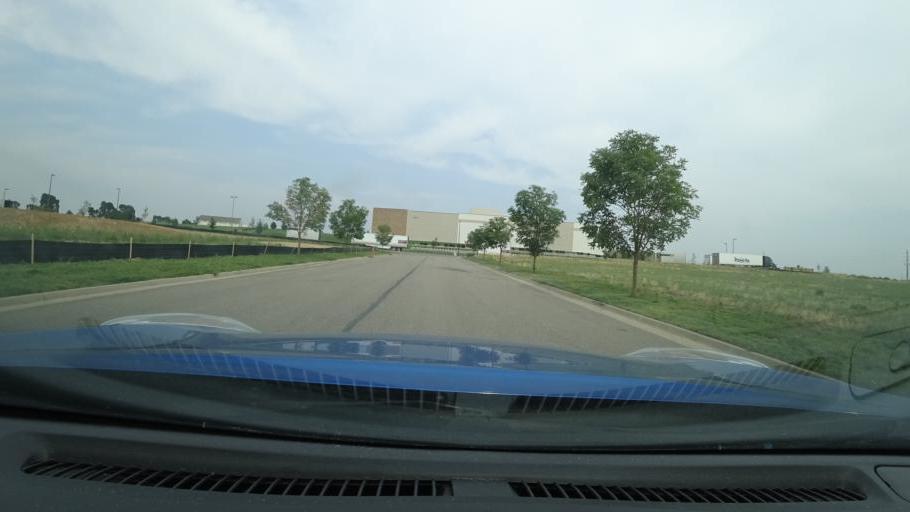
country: US
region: Colorado
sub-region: Adams County
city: Aurora
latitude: 39.7488
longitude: -104.7546
